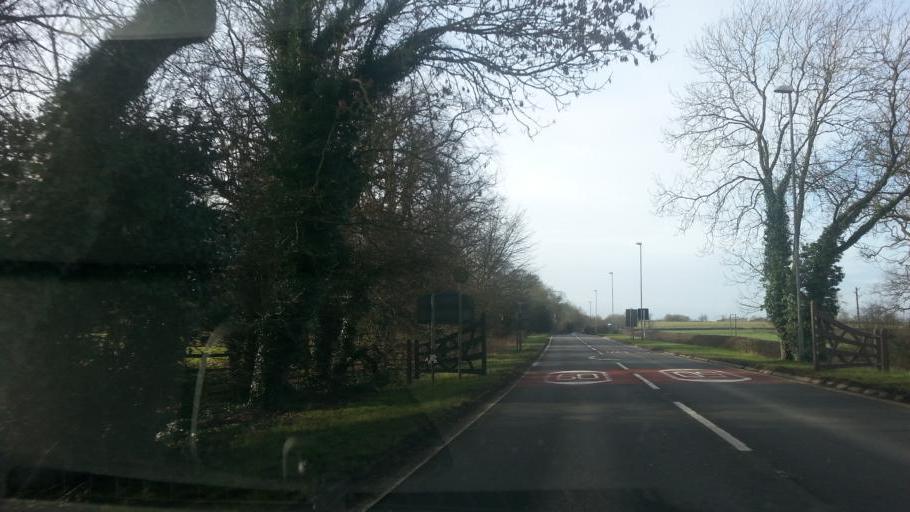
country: GB
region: England
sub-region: Leicestershire
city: Houghton on the Hill
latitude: 52.6179
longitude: -0.9032
